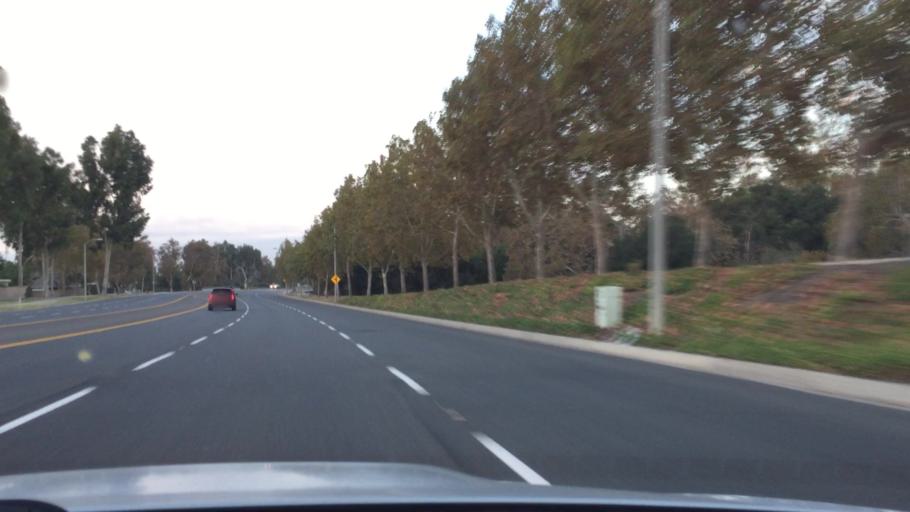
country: US
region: California
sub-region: Orange County
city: Lake Forest
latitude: 33.6465
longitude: -117.6639
